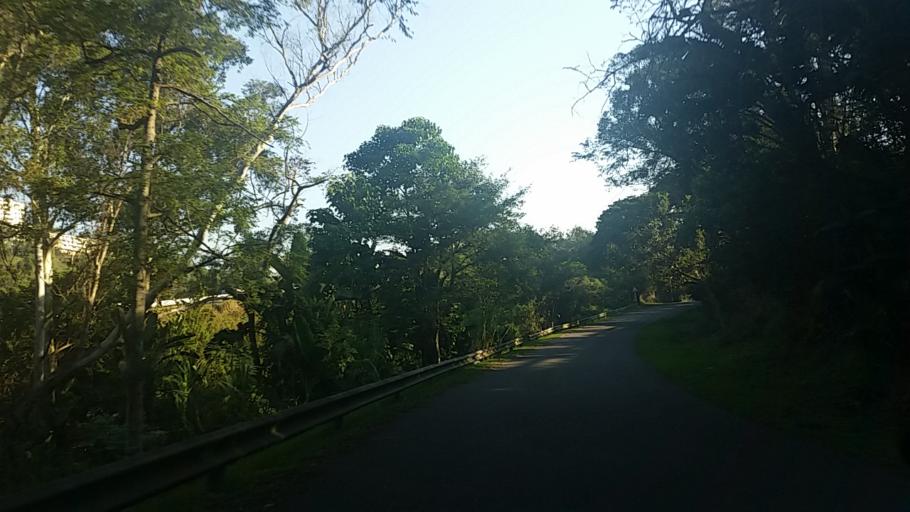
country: ZA
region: KwaZulu-Natal
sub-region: eThekwini Metropolitan Municipality
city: Berea
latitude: -29.8329
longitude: 30.8891
